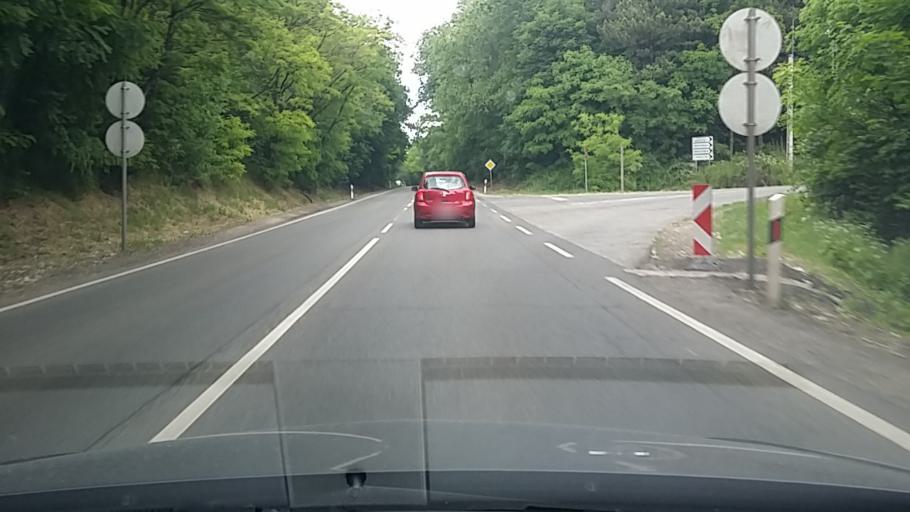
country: HU
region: Fejer
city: dunaujvaros
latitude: 46.9737
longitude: 18.9090
